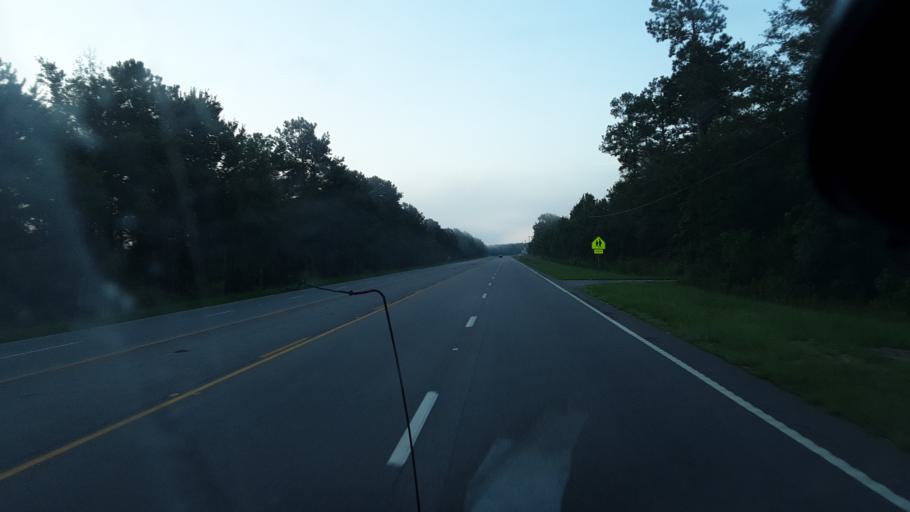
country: US
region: South Carolina
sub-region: Clarendon County
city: Manning
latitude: 33.7309
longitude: -80.2021
